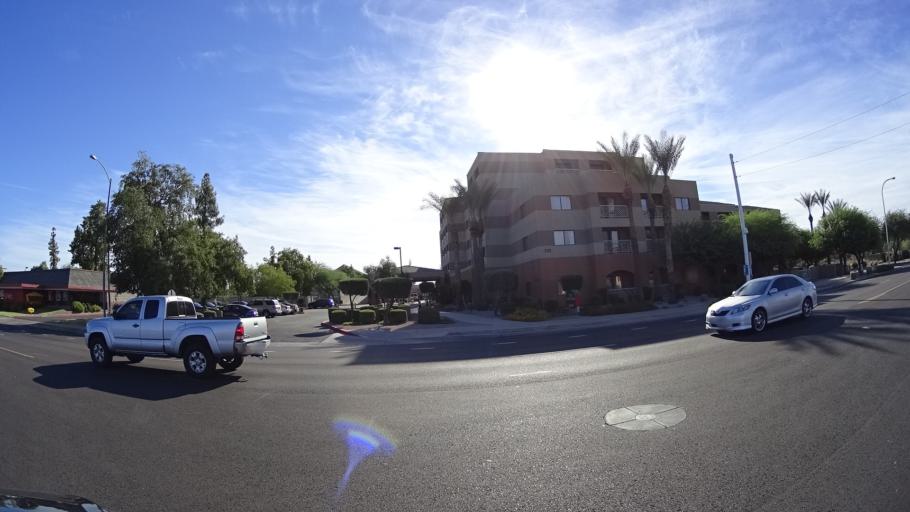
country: US
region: Arizona
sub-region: Maricopa County
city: Scottsdale
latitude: 33.4863
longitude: -111.9262
